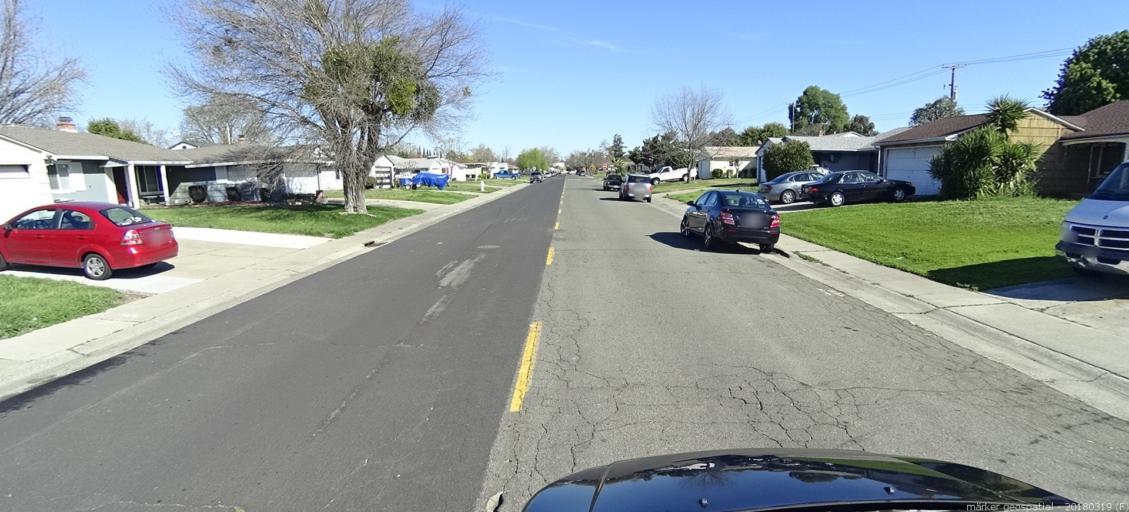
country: US
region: California
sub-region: Sacramento County
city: Parkway
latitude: 38.4877
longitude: -121.4414
